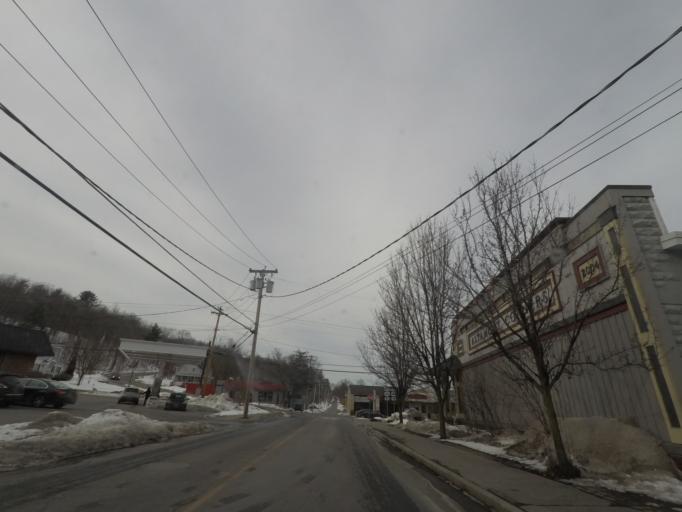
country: US
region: New York
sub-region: Albany County
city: Altamont
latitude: 42.7003
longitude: -74.0335
